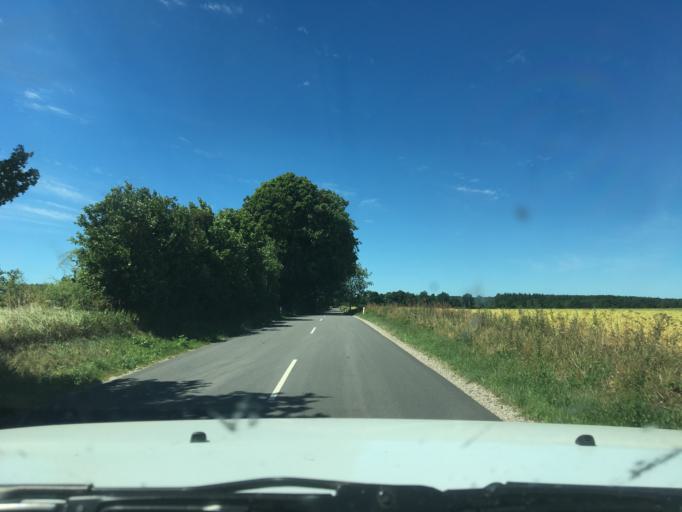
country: DK
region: Central Jutland
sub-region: Syddjurs Kommune
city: Hornslet
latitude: 56.3282
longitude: 10.3516
